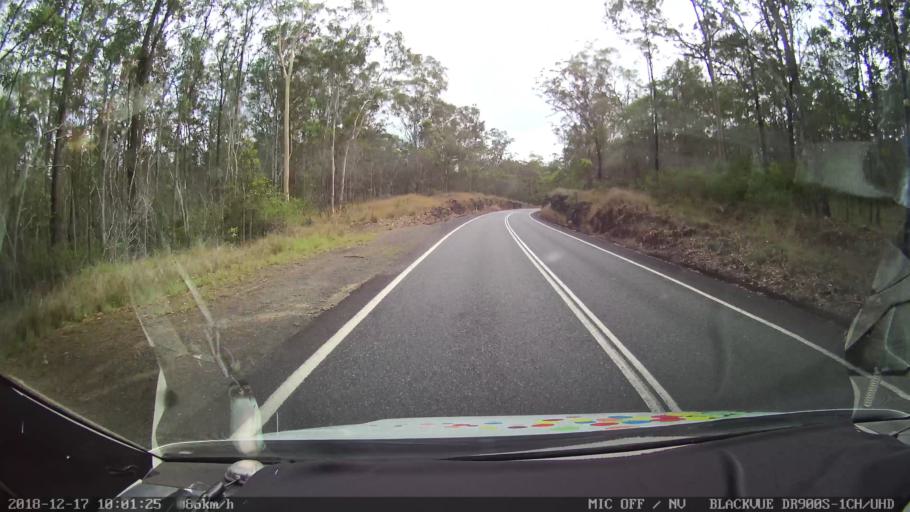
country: AU
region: New South Wales
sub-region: Tenterfield Municipality
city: Carrolls Creek
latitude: -28.9045
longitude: 152.4377
